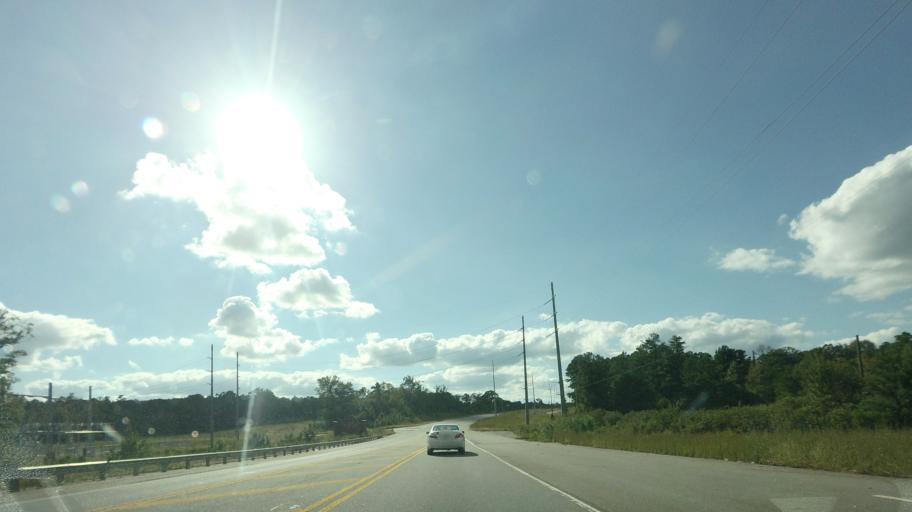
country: US
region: Georgia
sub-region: Lamar County
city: Barnesville
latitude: 33.0518
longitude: -84.1233
